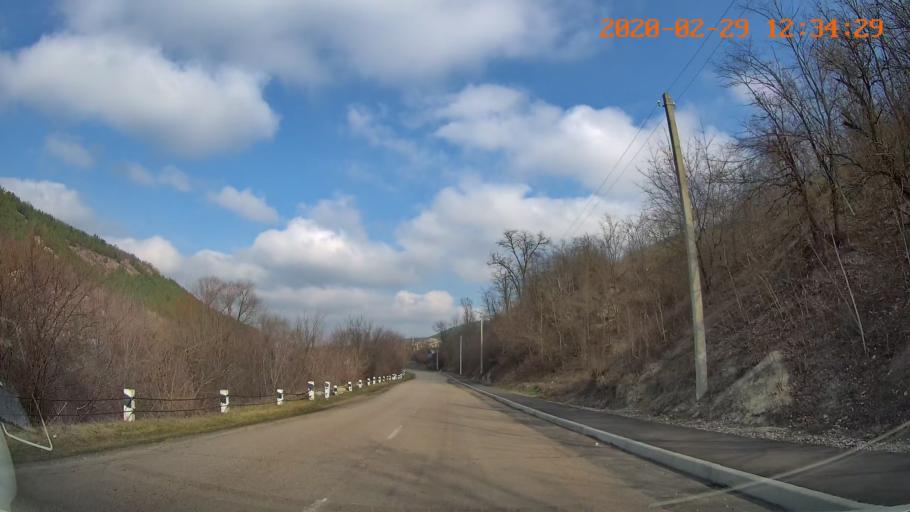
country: MD
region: Telenesti
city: Camenca
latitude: 48.0395
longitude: 28.7144
